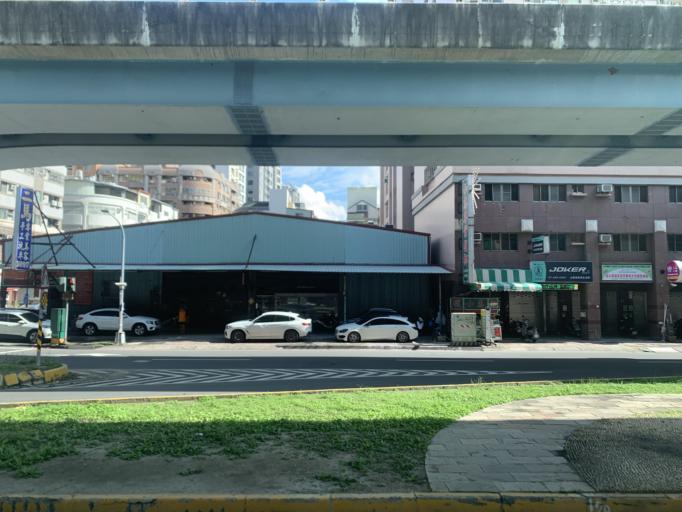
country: TW
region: Kaohsiung
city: Kaohsiung
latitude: 22.6817
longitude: 120.3095
